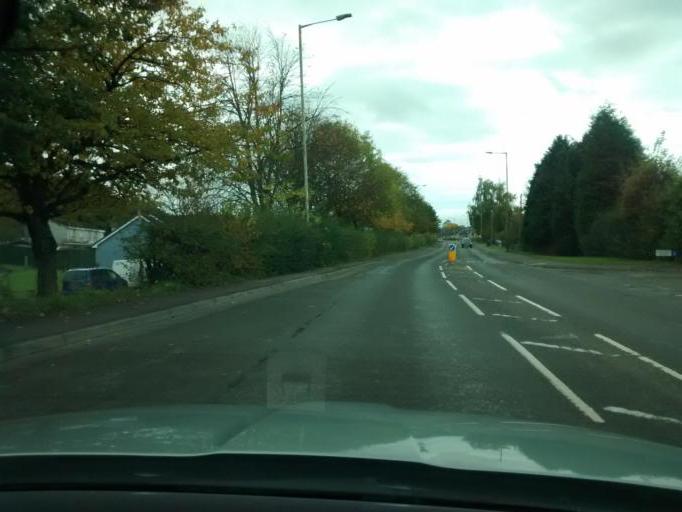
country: GB
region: Scotland
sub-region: Perth and Kinross
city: Luncarty
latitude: 56.4524
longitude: -3.4702
